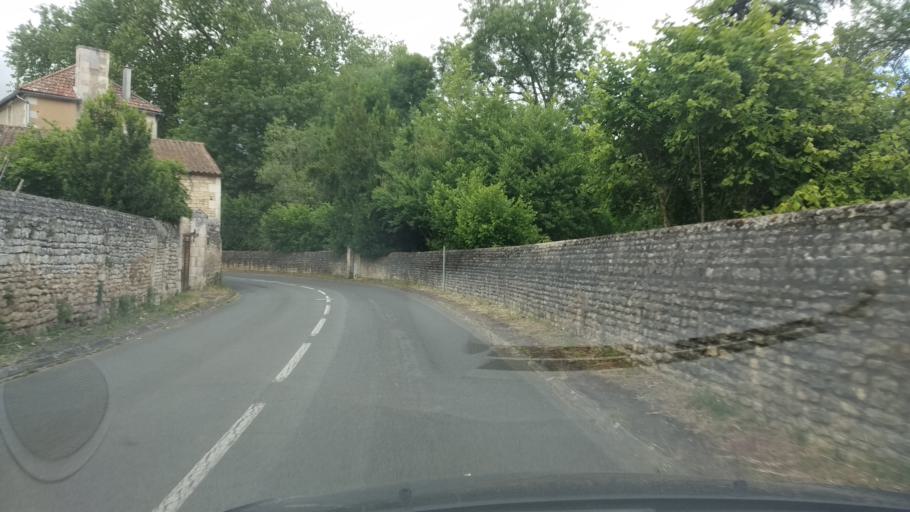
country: FR
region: Poitou-Charentes
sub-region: Departement de la Vienne
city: Vouille
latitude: 46.6367
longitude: 0.1684
